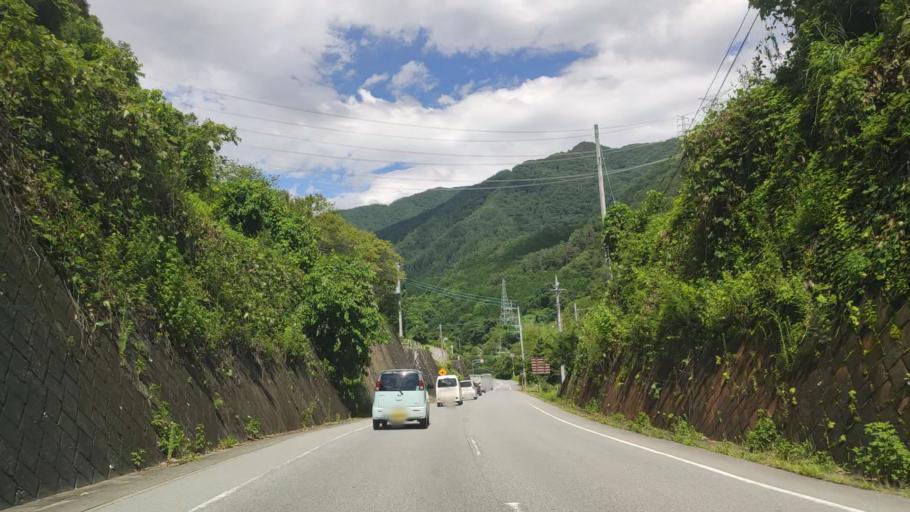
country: JP
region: Yamanashi
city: Enzan
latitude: 35.7587
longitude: 138.7286
